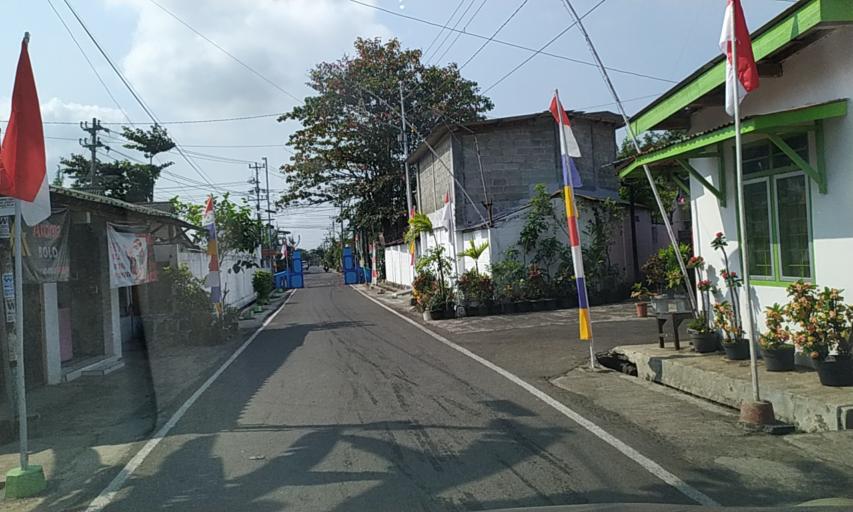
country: ID
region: Central Java
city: Karangbadar Kidul
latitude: -7.7283
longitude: 109.0001
